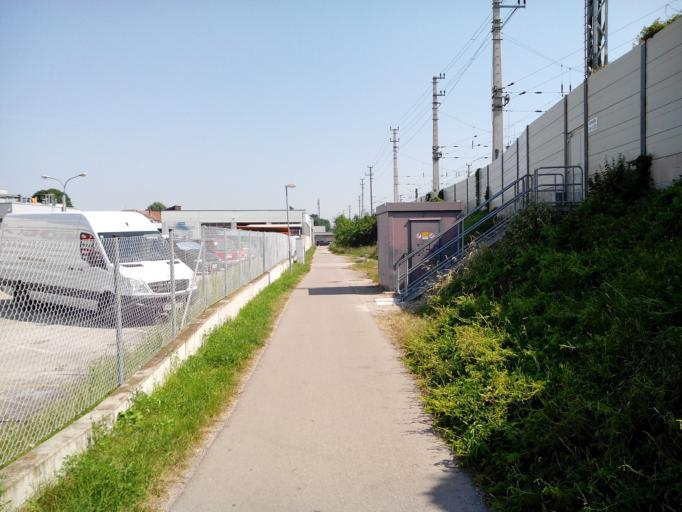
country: AT
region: Lower Austria
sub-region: Wiener Neustadt Stadt
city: Wiener Neustadt
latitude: 47.8135
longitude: 16.2342
